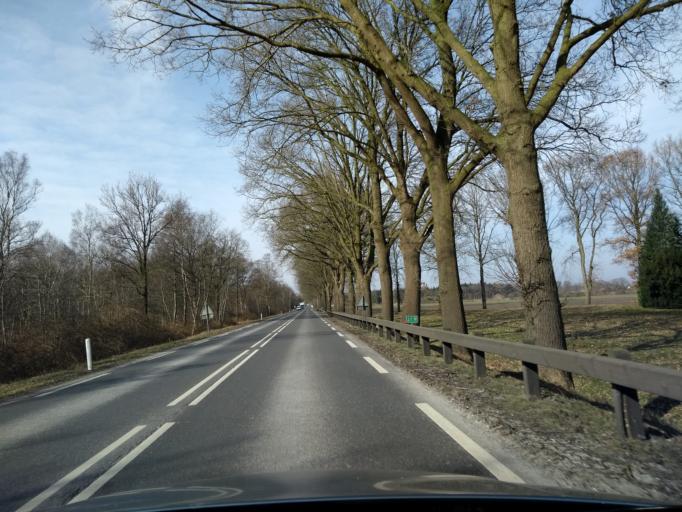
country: NL
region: Overijssel
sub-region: Gemeente Twenterand
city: Westerhaar-Vriezenveensewijk
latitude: 52.4904
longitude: 6.6824
